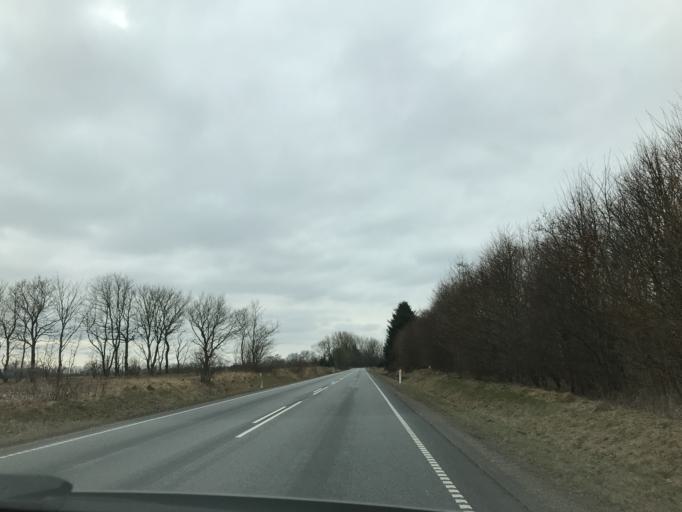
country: DK
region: South Denmark
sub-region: Varde Kommune
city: Olgod
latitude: 55.8140
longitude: 8.6647
